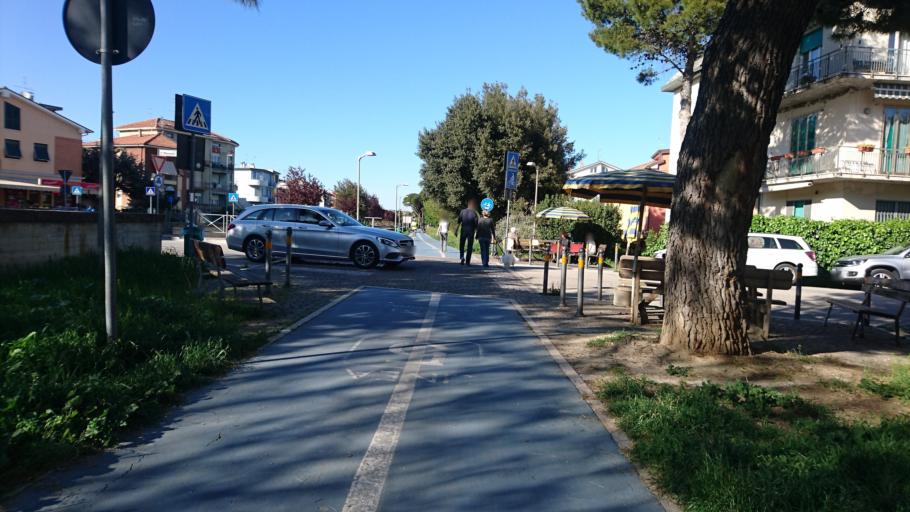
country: IT
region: The Marches
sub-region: Provincia di Pesaro e Urbino
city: Pesaro
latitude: 43.8978
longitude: 12.9117
